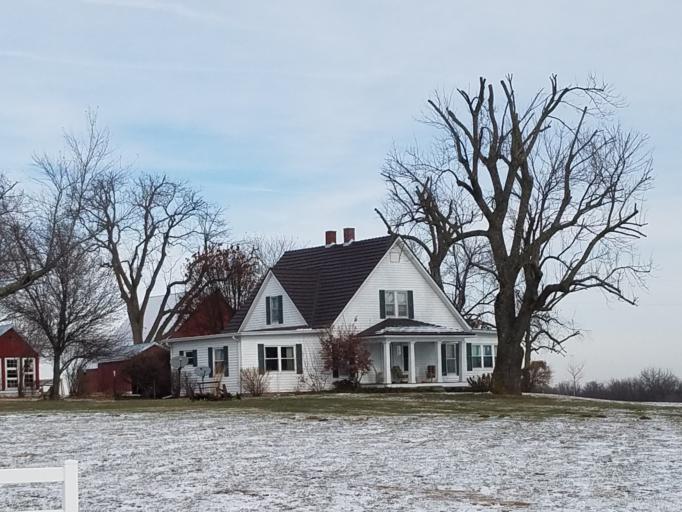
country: US
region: Missouri
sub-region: Lafayette County
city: Lexington
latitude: 39.1786
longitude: -93.7801
